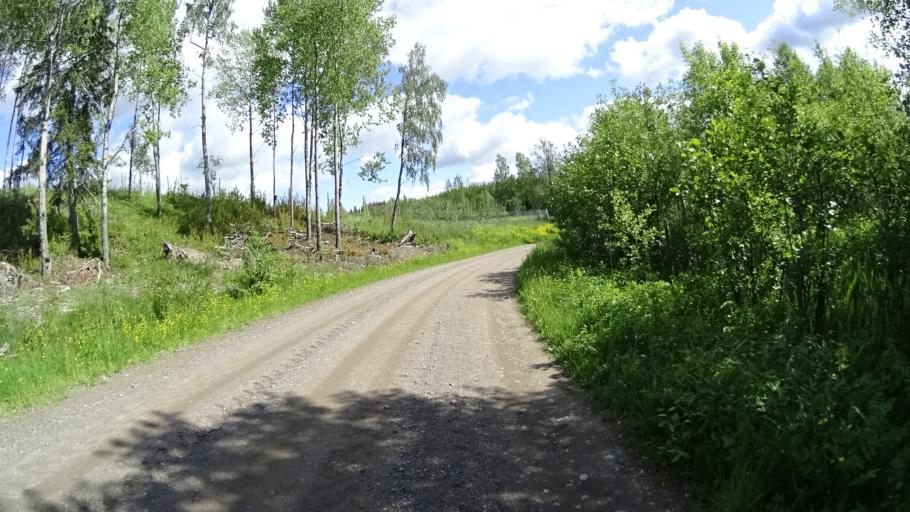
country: FI
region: Uusimaa
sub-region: Raaseporin
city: Karis
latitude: 60.1263
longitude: 23.6094
